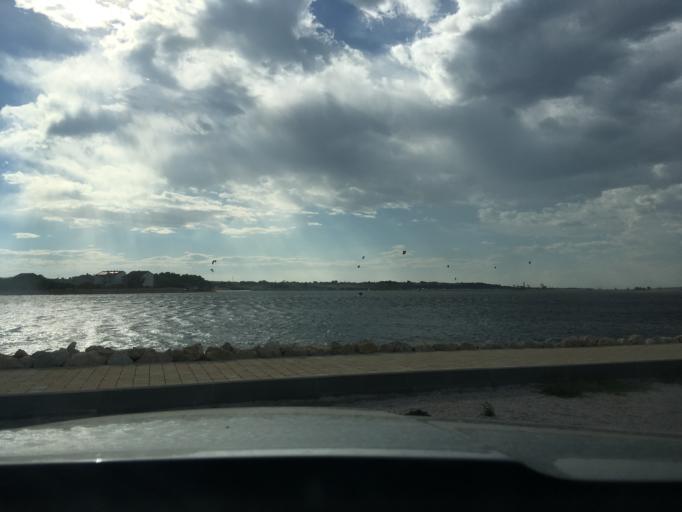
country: HR
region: Zadarska
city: Nin
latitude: 44.2454
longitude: 15.1893
